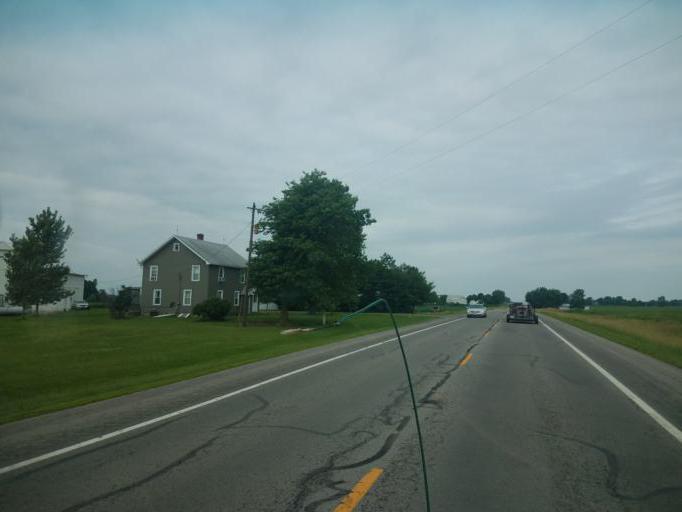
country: US
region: Ohio
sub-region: Hardin County
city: Kenton
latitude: 40.6982
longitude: -83.7151
